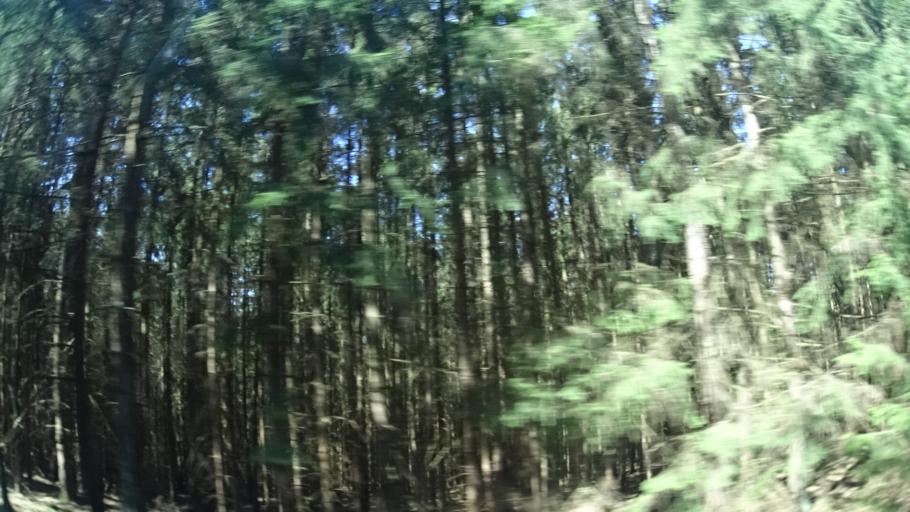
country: DE
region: Thuringia
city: Hildburghausen
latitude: 50.4549
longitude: 10.7770
